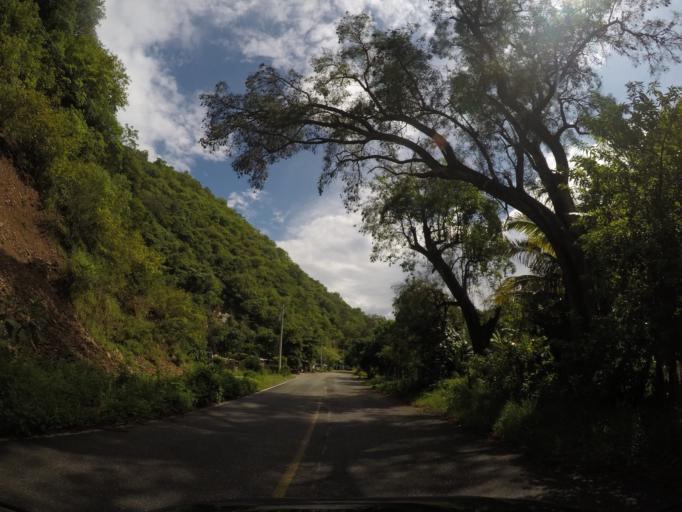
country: MX
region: Oaxaca
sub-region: San Jeronimo Coatlan
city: San Cristobal Honduras
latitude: 16.3596
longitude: -97.0917
